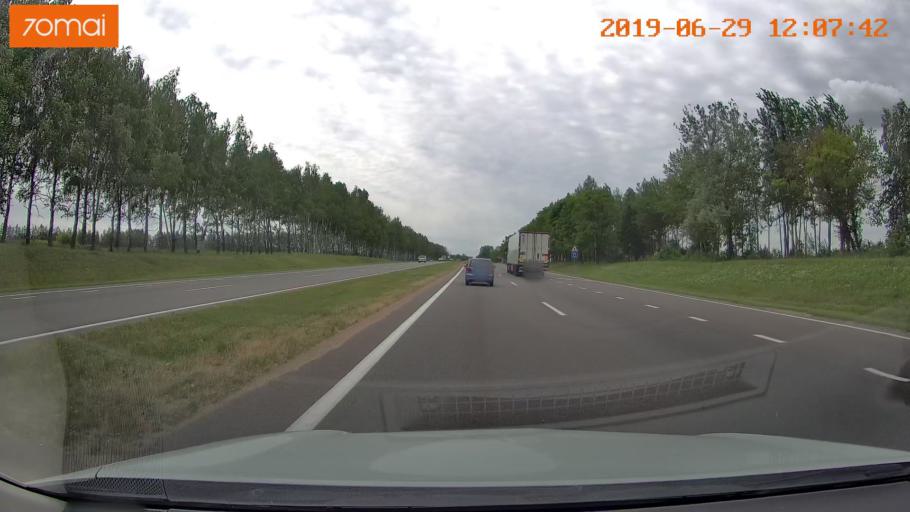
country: BY
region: Minsk
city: Samakhvalavichy
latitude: 53.7174
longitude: 27.5187
